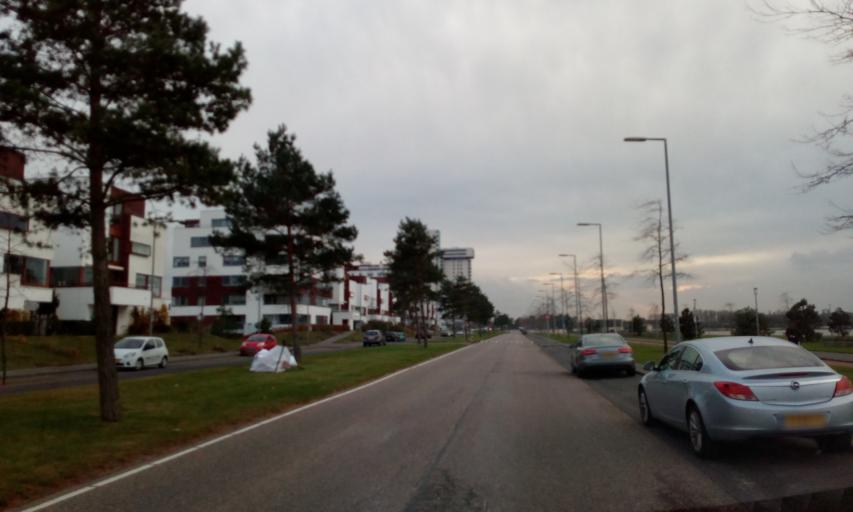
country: NL
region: South Holland
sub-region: Gemeente Lansingerland
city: Bleiswijk
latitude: 51.9852
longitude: 4.5818
